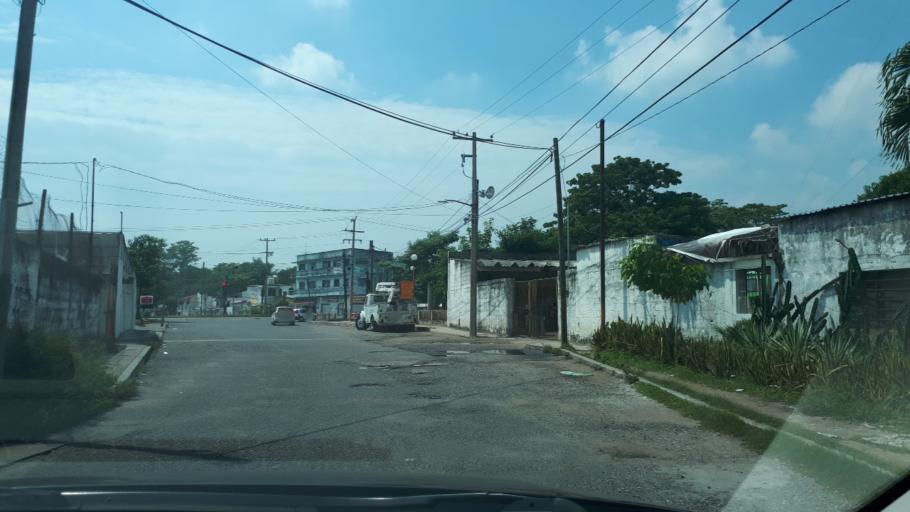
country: MX
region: Tabasco
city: Comalcalco
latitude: 18.2679
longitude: -93.2197
